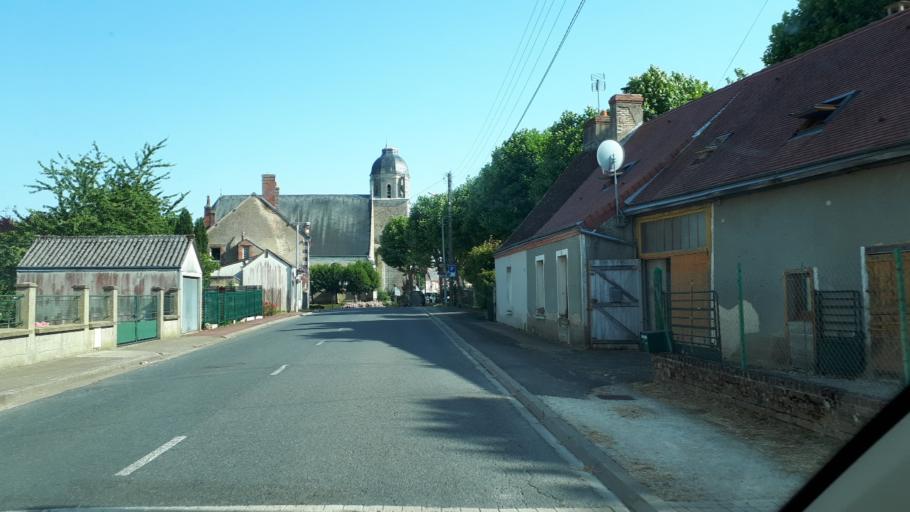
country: FR
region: Centre
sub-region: Departement du Loir-et-Cher
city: La Ville-aux-Clercs
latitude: 47.9199
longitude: 1.0850
